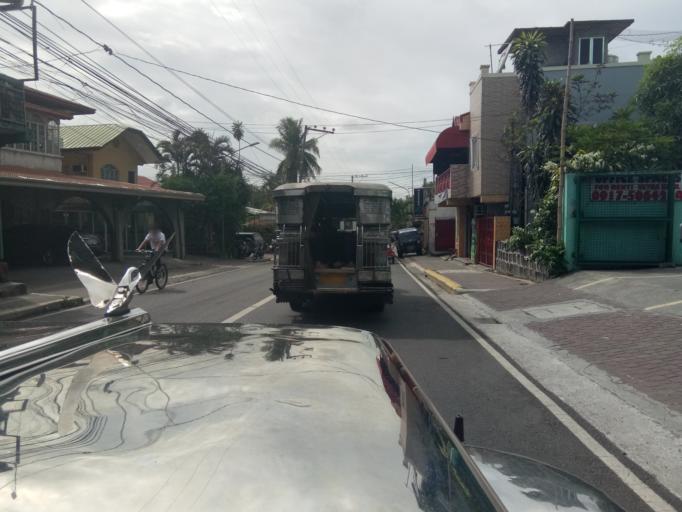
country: PH
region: Calabarzon
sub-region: Province of Cavite
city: Dasmarinas
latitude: 14.3175
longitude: 120.9430
